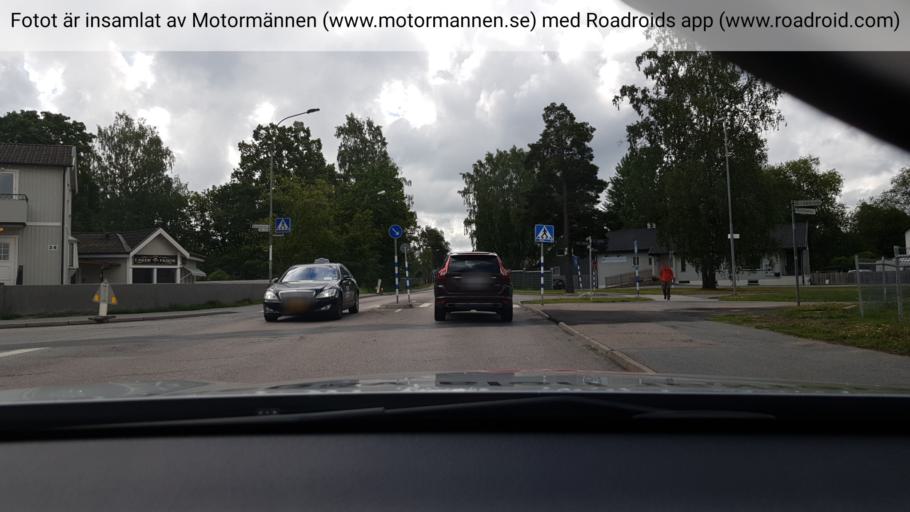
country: SE
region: Stockholm
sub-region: Haninge Kommun
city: Haninge
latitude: 59.1736
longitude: 18.1461
